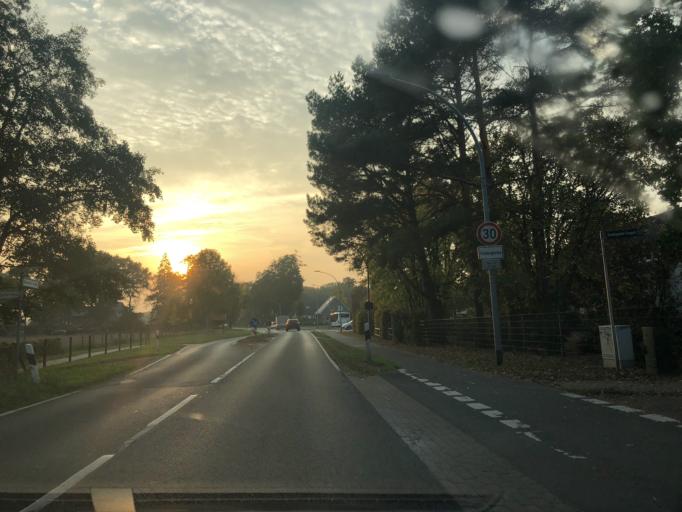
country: DE
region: Lower Saxony
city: Wardenburg
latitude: 53.0900
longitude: 8.1868
